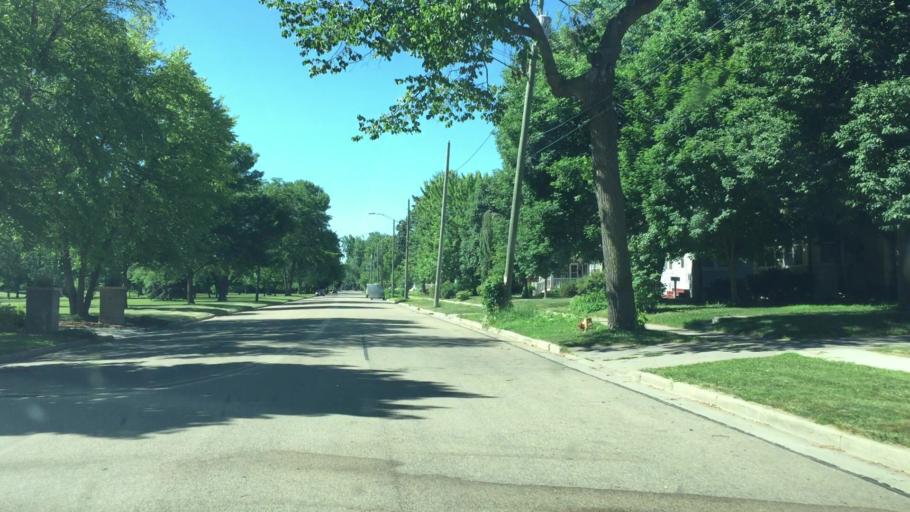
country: US
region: Wisconsin
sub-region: Winnebago County
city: Menasha
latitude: 44.1971
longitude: -88.4420
